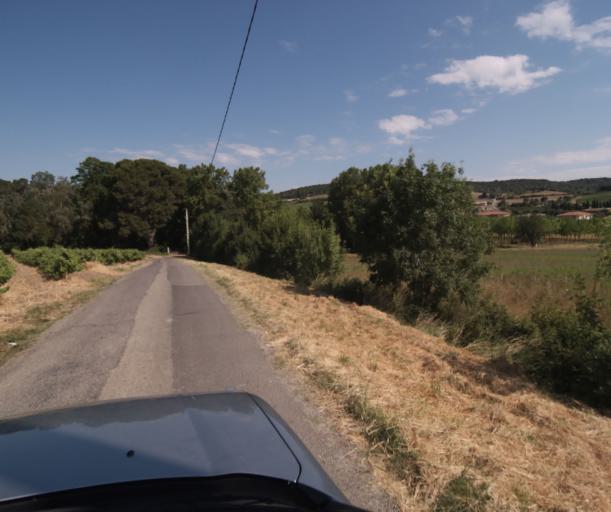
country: FR
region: Languedoc-Roussillon
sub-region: Departement de l'Aude
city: Limoux
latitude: 43.0668
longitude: 2.2044
